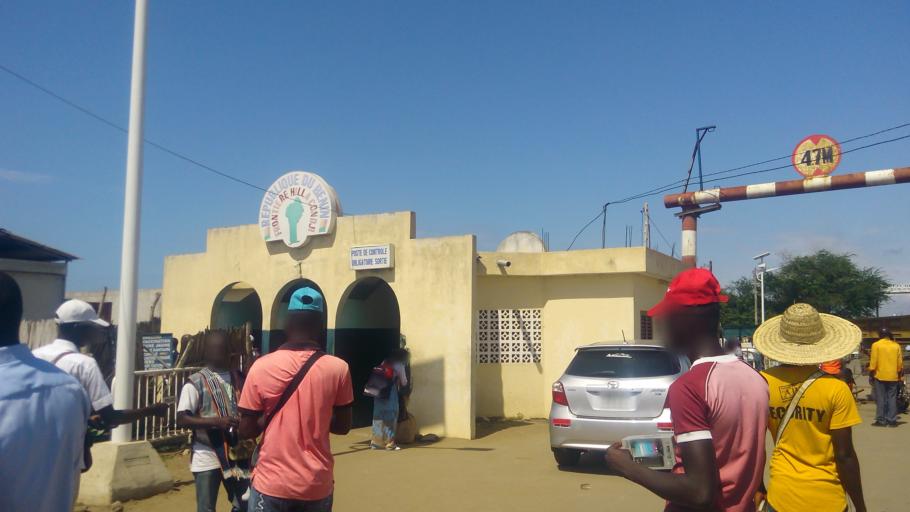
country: TG
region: Maritime
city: Aneho
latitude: 6.2407
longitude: 1.6301
